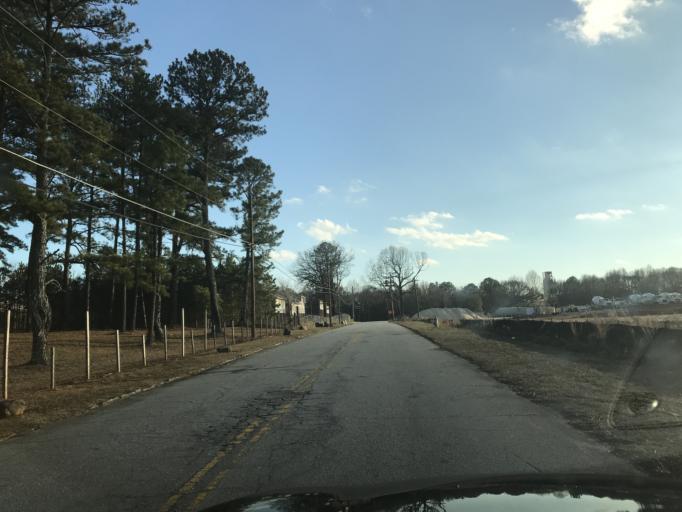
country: US
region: Georgia
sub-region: Fulton County
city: College Park
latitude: 33.6258
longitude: -84.4841
